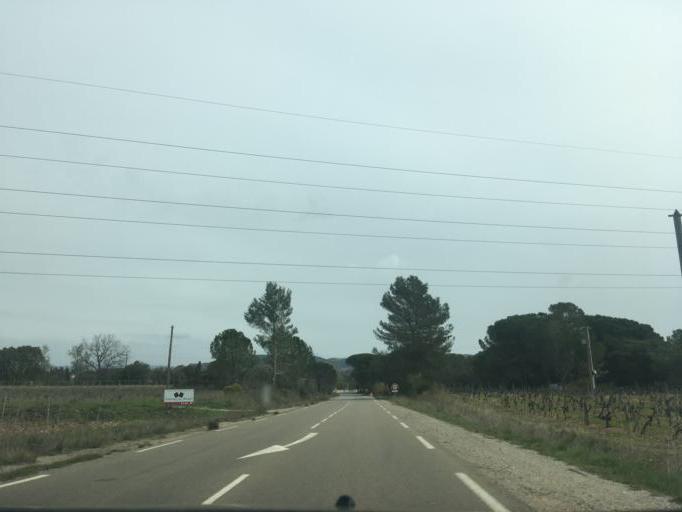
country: FR
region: Provence-Alpes-Cote d'Azur
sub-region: Departement du Var
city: Le Muy
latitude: 43.4939
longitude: 6.5727
